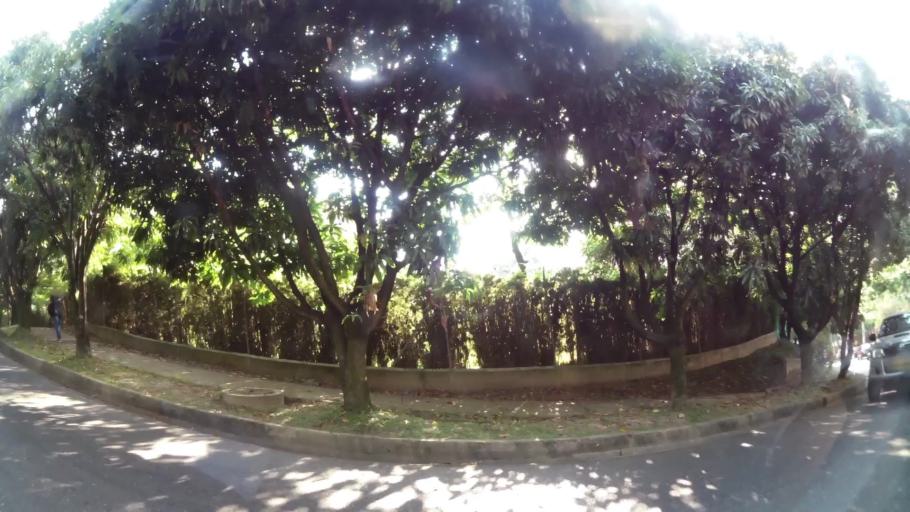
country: CO
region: Antioquia
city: Medellin
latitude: 6.2253
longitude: -75.5668
